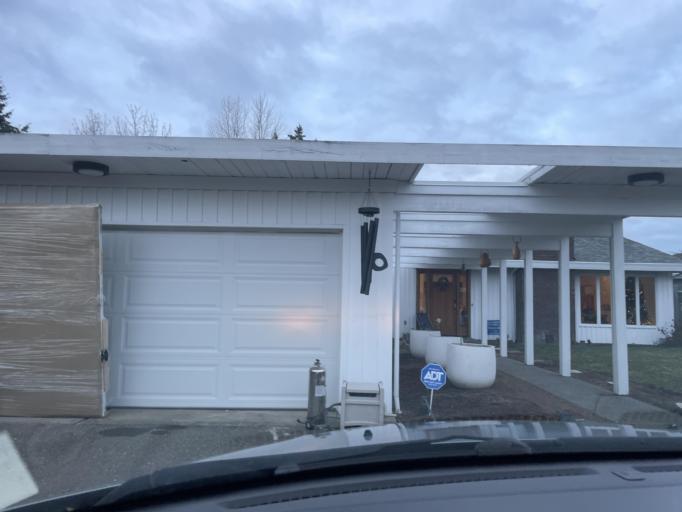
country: US
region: Washington
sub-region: King County
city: Newport
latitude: 47.5926
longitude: -122.1790
